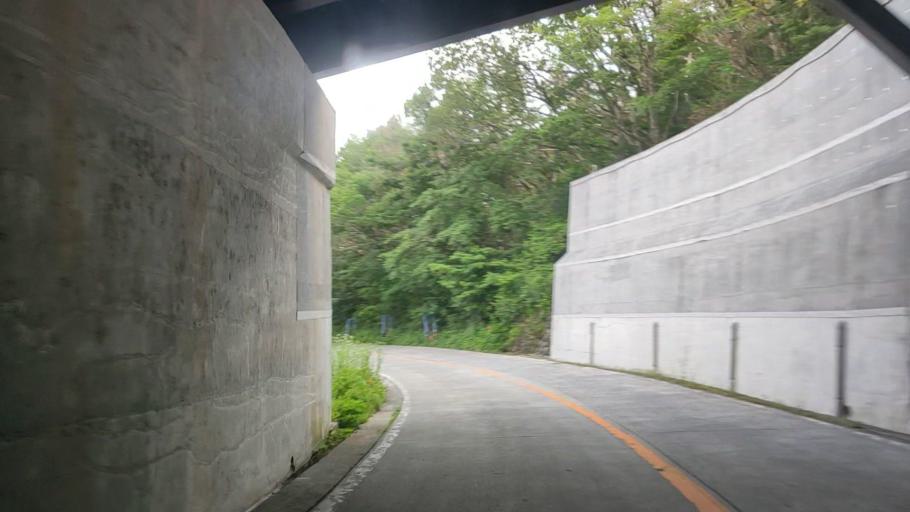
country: JP
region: Tottori
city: Yonago
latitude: 35.3653
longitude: 133.5210
